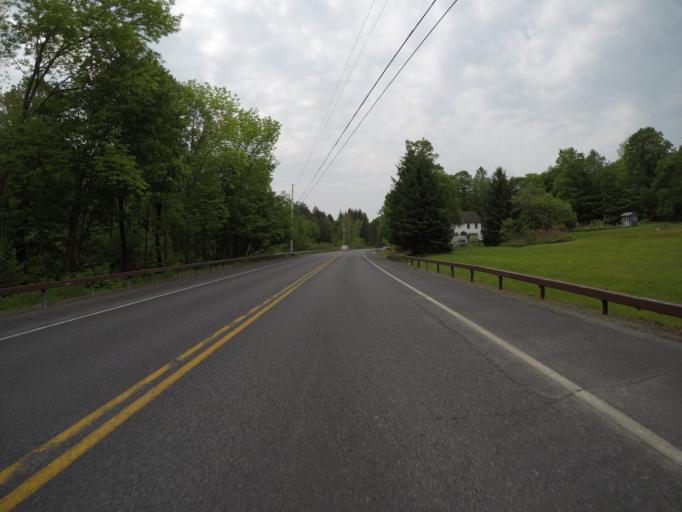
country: US
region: New York
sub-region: Sullivan County
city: Livingston Manor
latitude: 41.9883
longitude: -74.8938
